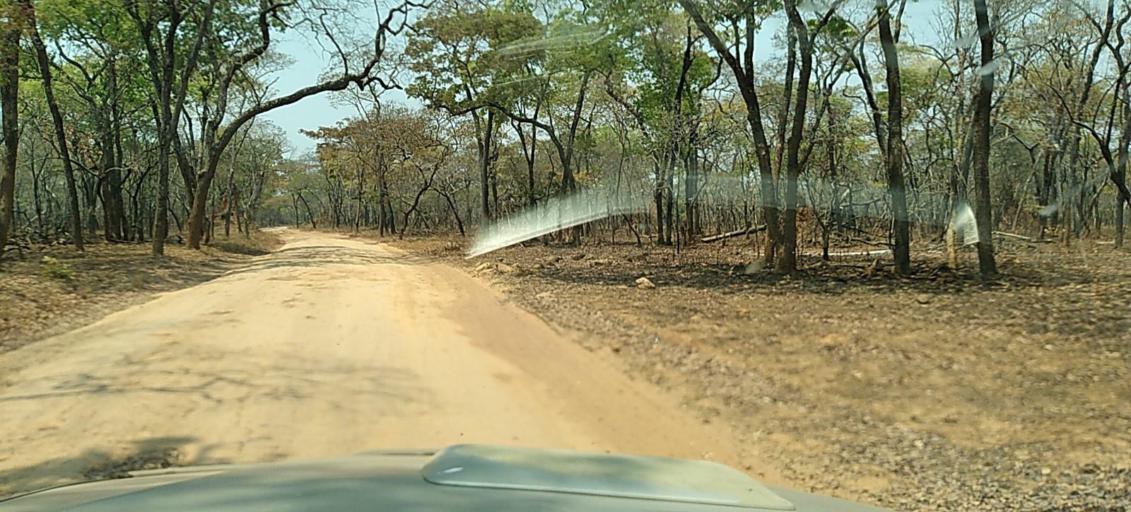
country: ZM
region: North-Western
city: Kasempa
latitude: -13.6075
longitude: 26.1809
